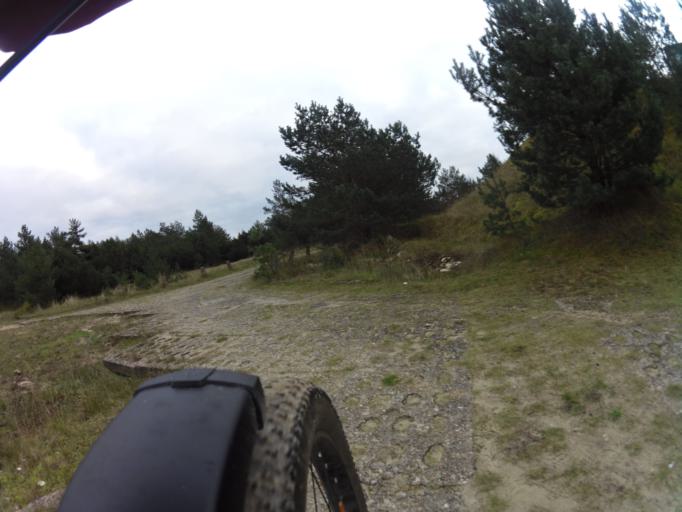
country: PL
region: Pomeranian Voivodeship
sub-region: Powiat leborski
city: Leba
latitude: 54.7697
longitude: 17.5932
